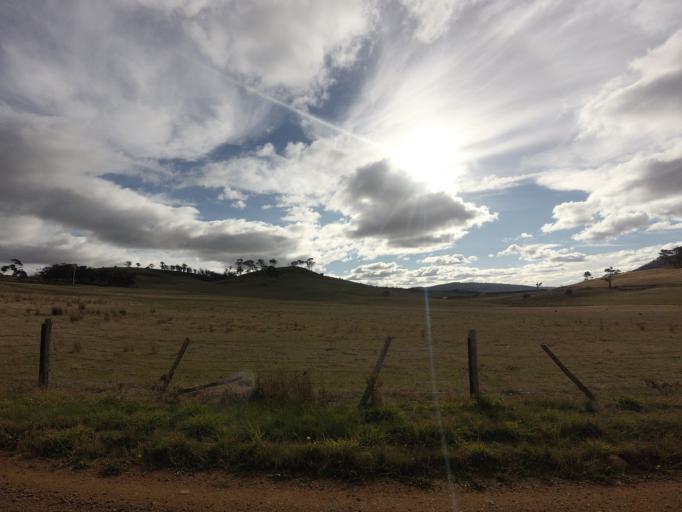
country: AU
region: Tasmania
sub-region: Brighton
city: Bridgewater
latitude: -42.4900
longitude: 147.3307
